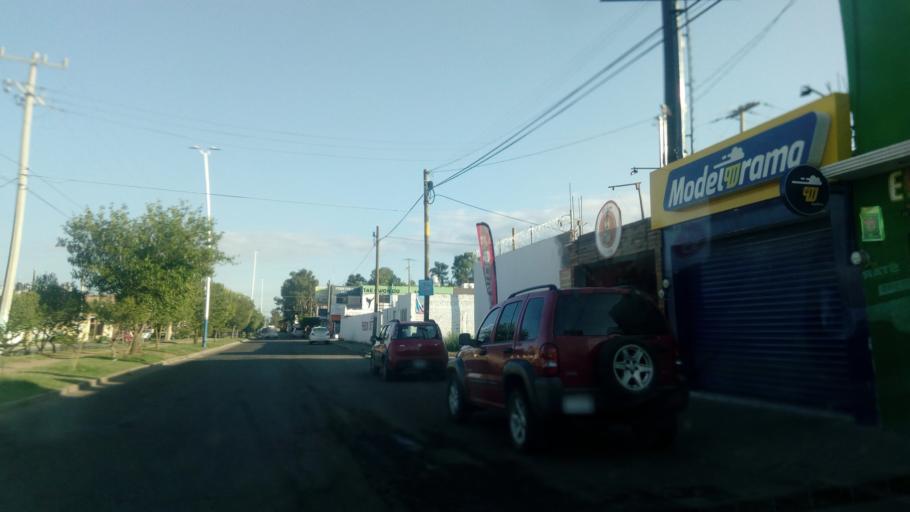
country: MX
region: Durango
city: Victoria de Durango
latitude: 24.0445
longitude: -104.6130
